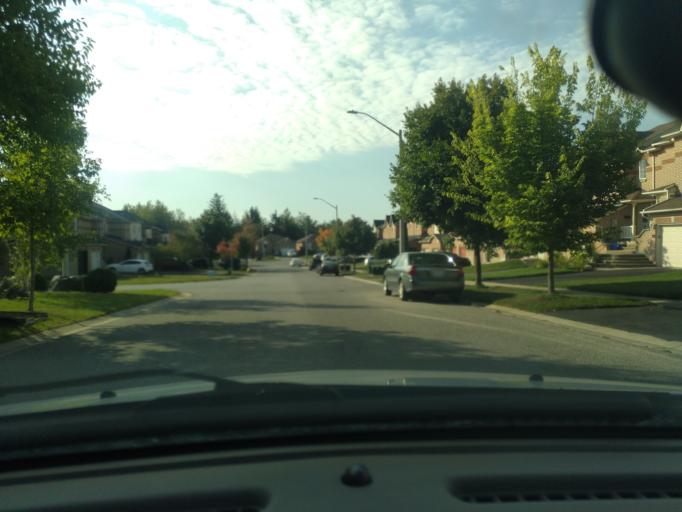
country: CA
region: Ontario
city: Innisfil
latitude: 44.3486
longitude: -79.6631
